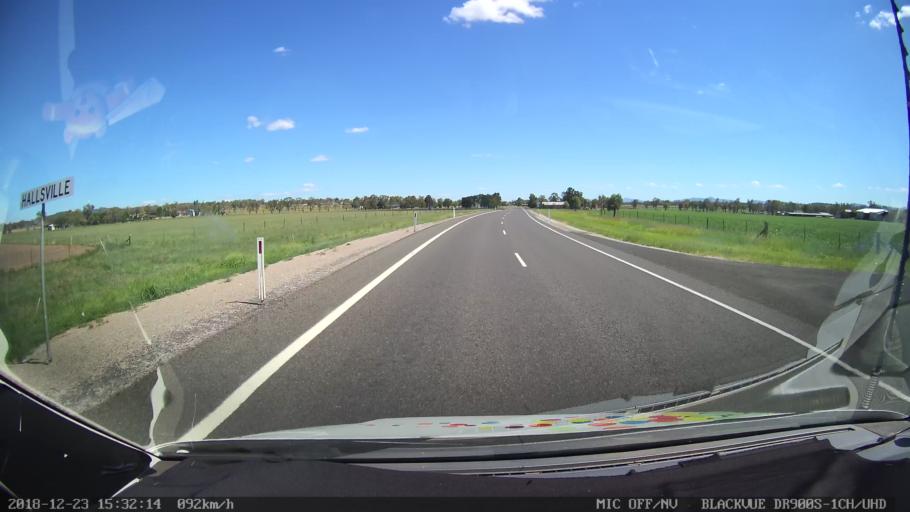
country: AU
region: New South Wales
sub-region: Tamworth Municipality
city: East Tamworth
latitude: -30.9827
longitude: 150.8701
